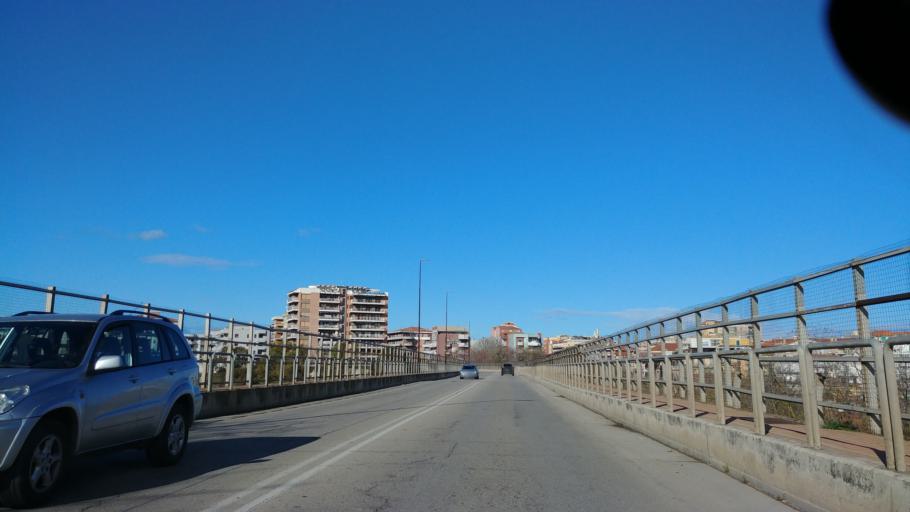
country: IT
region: Molise
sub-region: Provincia di Campobasso
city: Termoli
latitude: 41.9947
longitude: 14.9974
